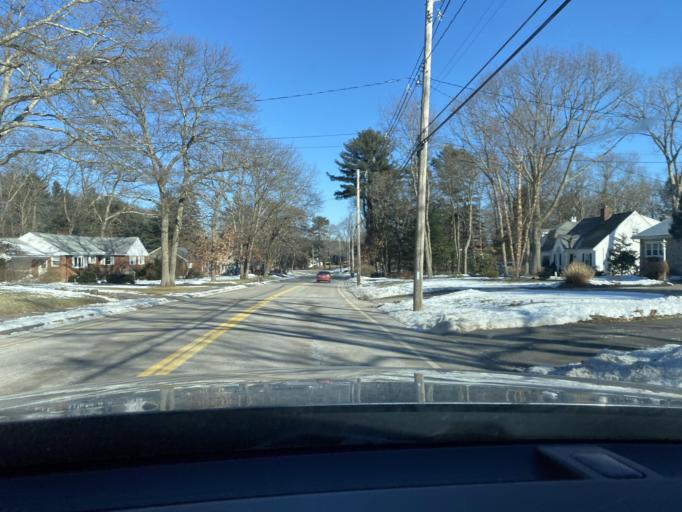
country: US
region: Massachusetts
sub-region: Norfolk County
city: Walpole
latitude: 42.1473
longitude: -71.2189
